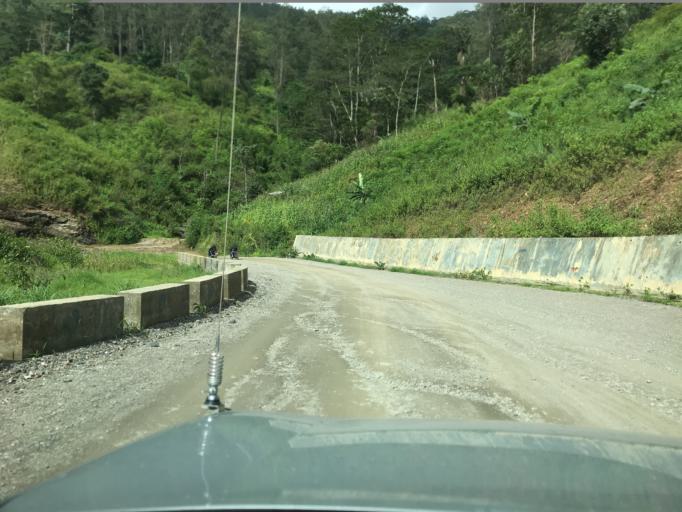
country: TL
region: Aileu
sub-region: Aileu Villa
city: Aileu
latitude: -8.6615
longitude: 125.5502
